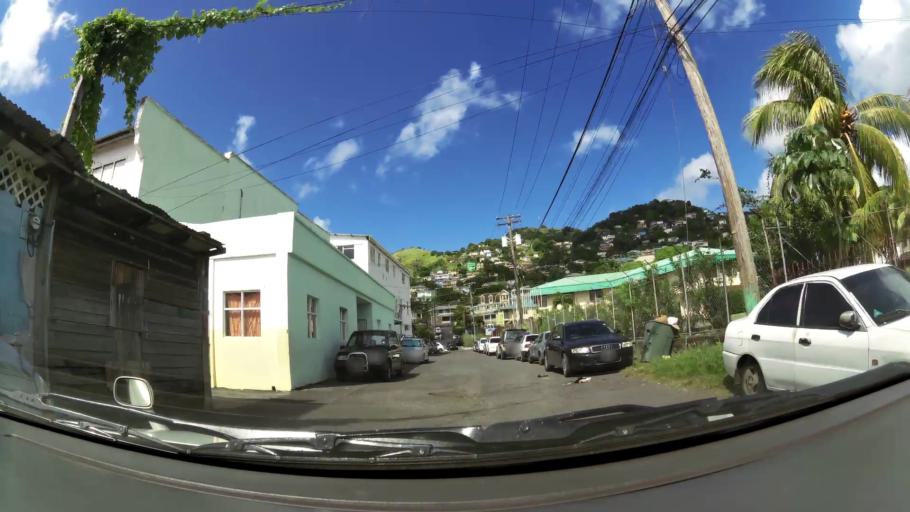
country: VC
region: Saint George
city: Kingstown
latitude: 13.1610
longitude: -61.2290
